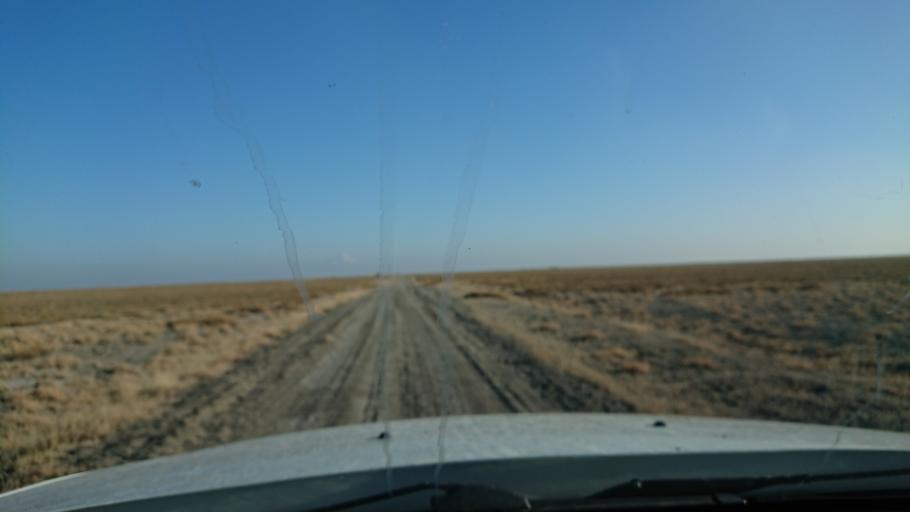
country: TR
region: Aksaray
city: Sultanhani
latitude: 38.3993
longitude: 33.5837
